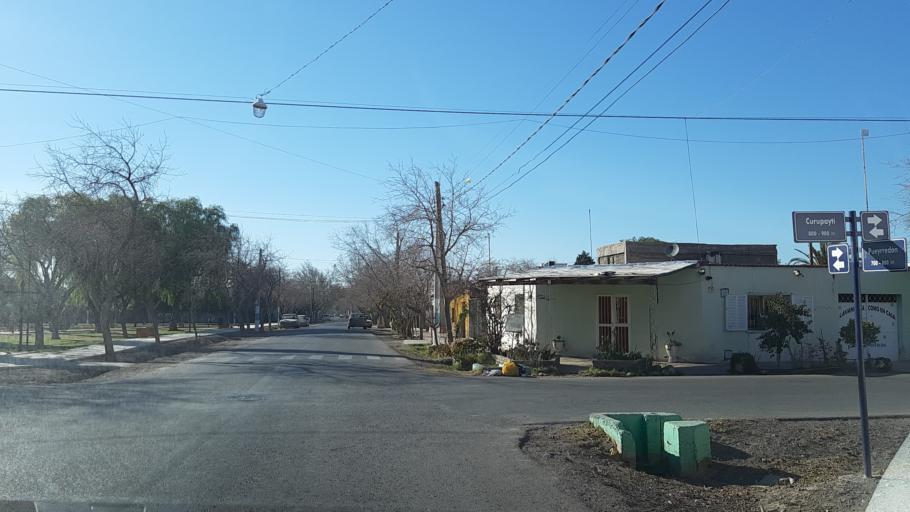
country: AR
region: San Juan
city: San Juan
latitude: -31.5378
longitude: -68.5758
